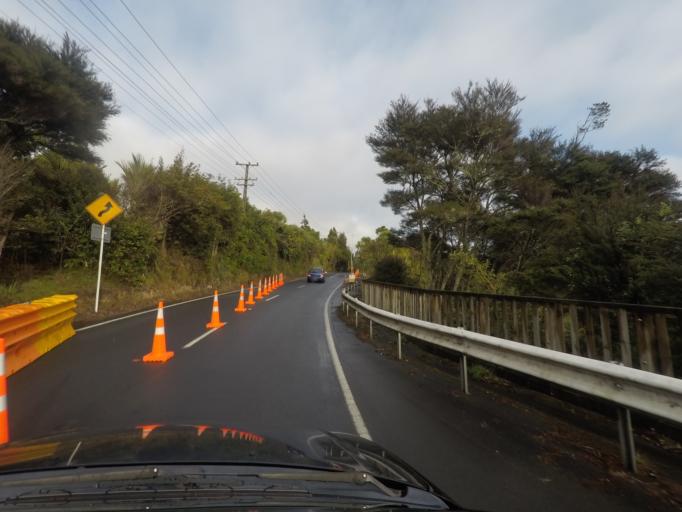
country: NZ
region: Auckland
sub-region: Auckland
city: Waitakere
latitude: -36.9171
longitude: 174.5957
